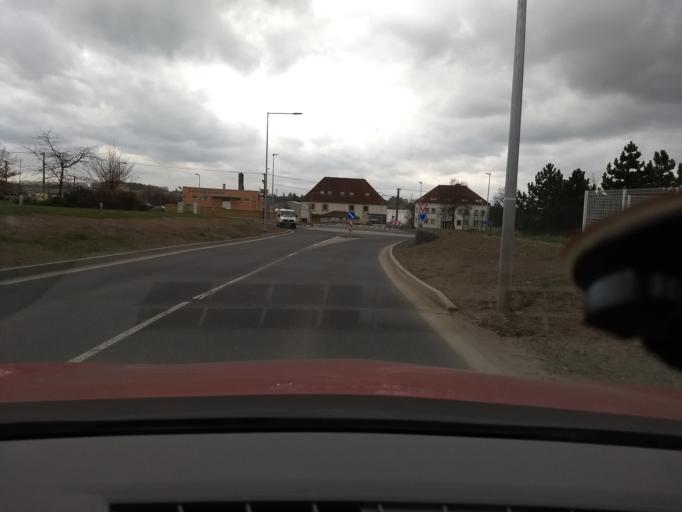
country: CZ
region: Central Bohemia
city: Unhost'
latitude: 50.1187
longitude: 14.1294
